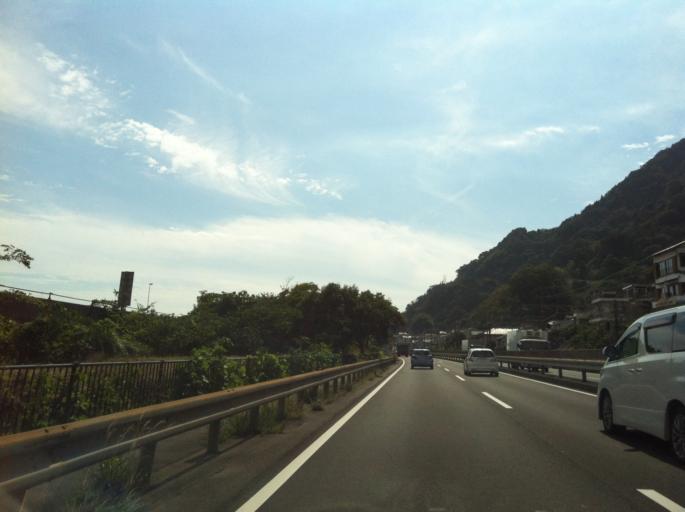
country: JP
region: Shizuoka
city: Fujinomiya
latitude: 35.0870
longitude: 138.5486
